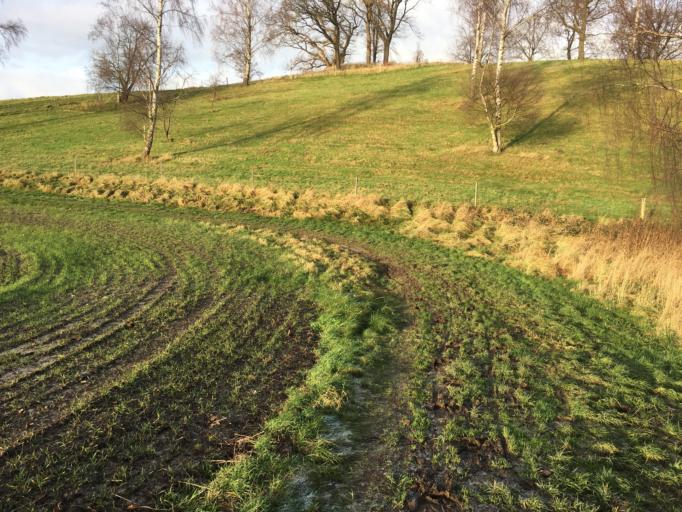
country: DK
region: Capital Region
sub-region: Fureso Kommune
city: Farum
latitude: 55.7920
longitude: 12.3425
